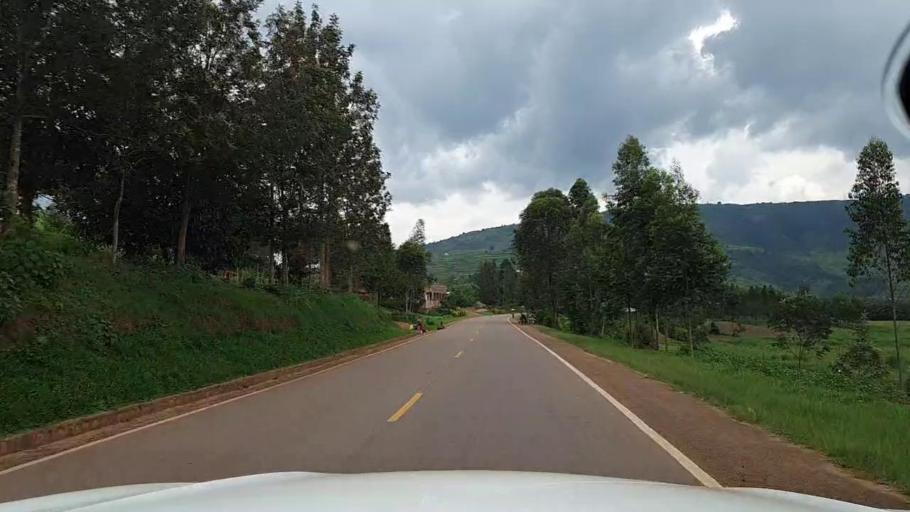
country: RW
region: Kigali
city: Kigali
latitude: -1.7847
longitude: 30.1296
